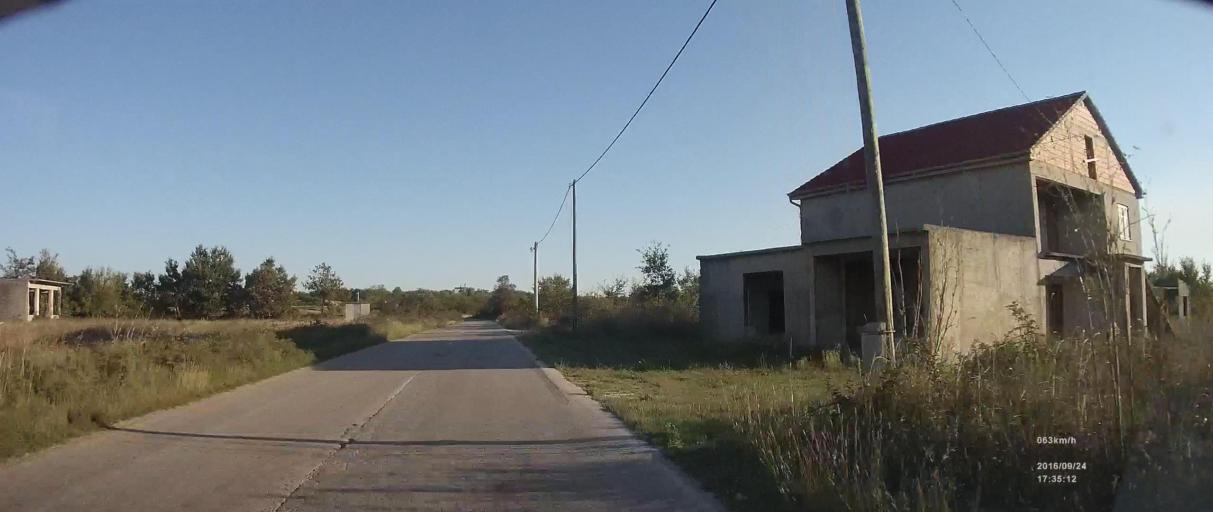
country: HR
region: Zadarska
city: Posedarje
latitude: 44.1621
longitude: 15.4655
